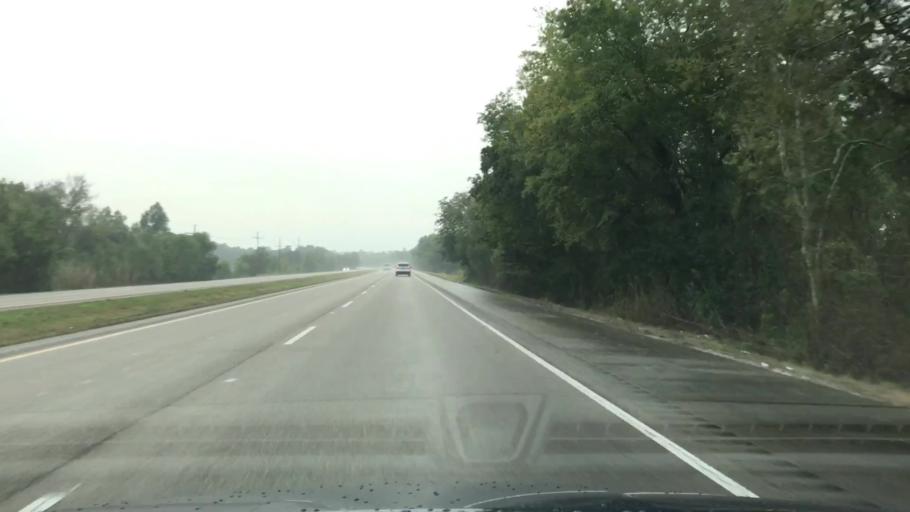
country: US
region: Louisiana
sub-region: Saint Charles Parish
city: Paradis
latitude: 29.8616
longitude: -90.4463
